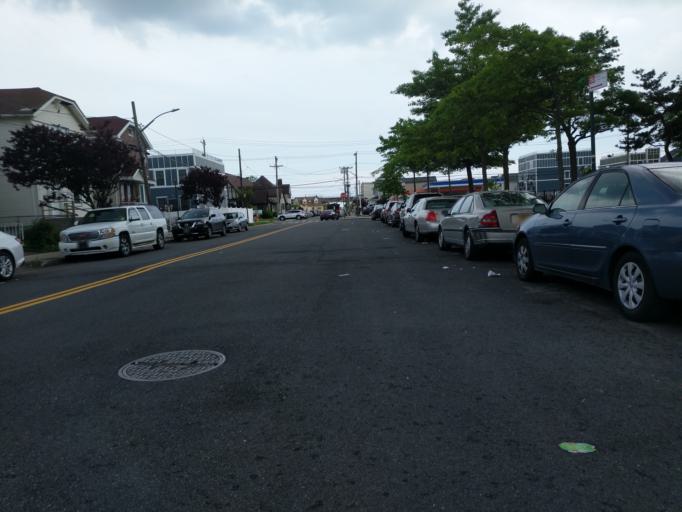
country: US
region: New York
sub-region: Nassau County
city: Inwood
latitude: 40.5967
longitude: -73.7708
